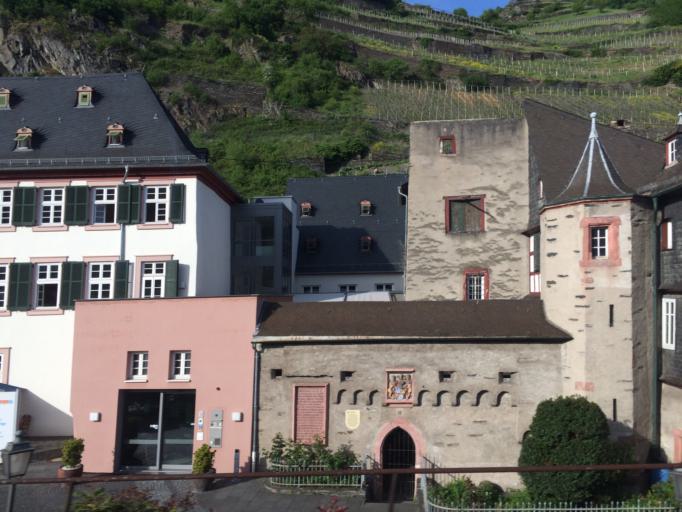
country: DE
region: Rheinland-Pfalz
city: Kaub
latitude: 50.0864
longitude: 7.7640
